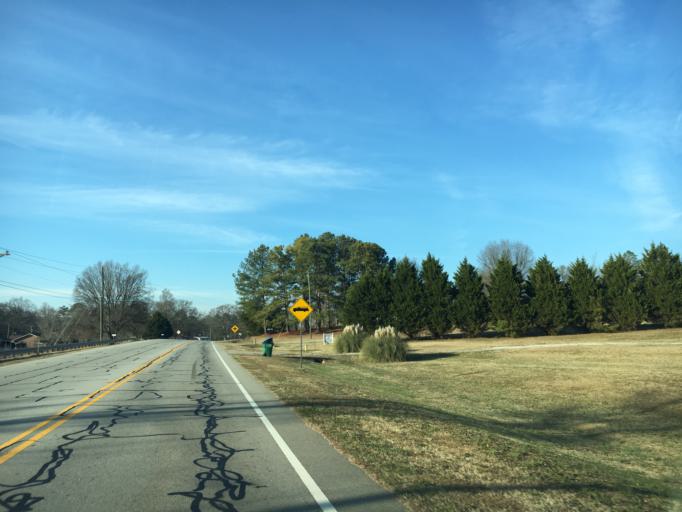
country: US
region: Georgia
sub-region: Franklin County
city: Lavonia
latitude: 34.4372
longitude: -83.0333
